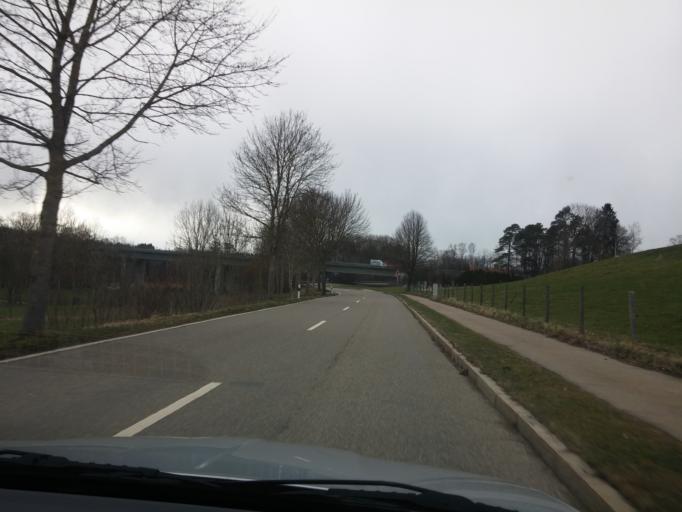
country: DE
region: Bavaria
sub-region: Swabia
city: Buxheim
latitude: 47.9887
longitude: 10.1399
